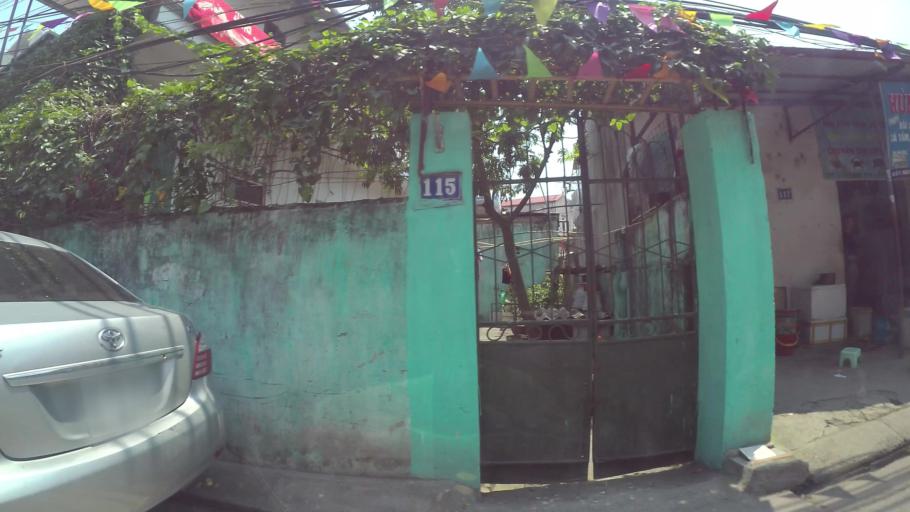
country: VN
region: Ha Noi
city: Hoan Kiem
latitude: 21.0231
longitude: 105.8921
